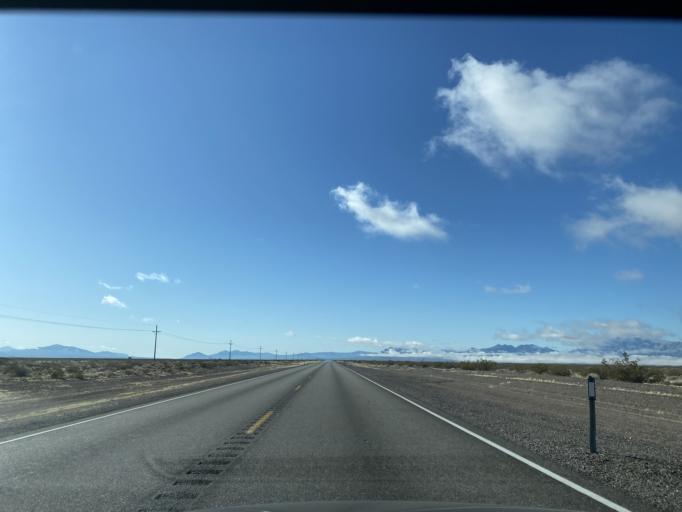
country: US
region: Nevada
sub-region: Nye County
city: Beatty
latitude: 36.6146
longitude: -116.4055
